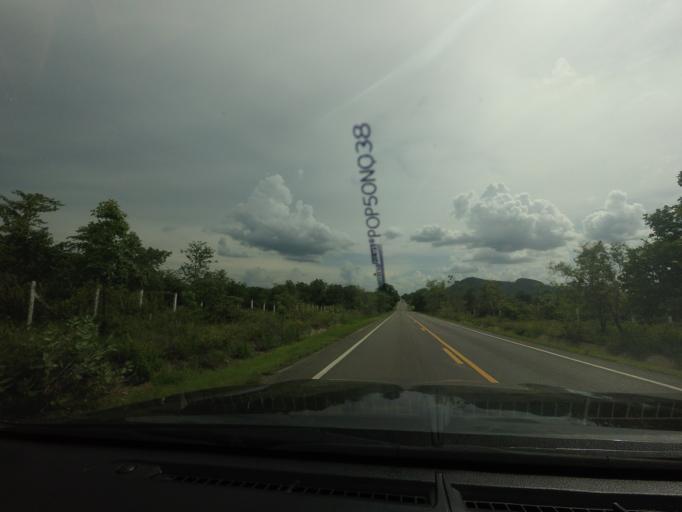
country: TH
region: Kanchanaburi
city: Kanchanaburi
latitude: 14.1481
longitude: 99.4199
